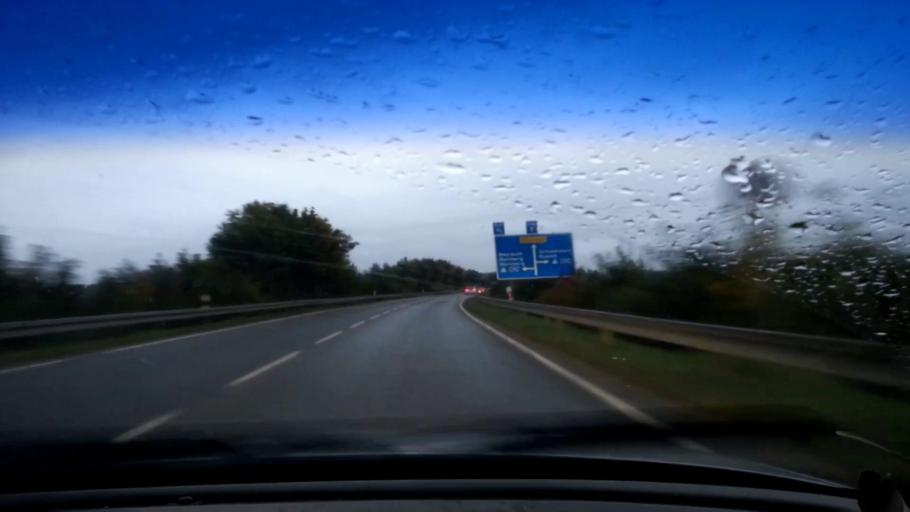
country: DE
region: Bavaria
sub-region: Upper Franconia
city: Viereth-Trunstadt
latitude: 49.9293
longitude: 10.7756
